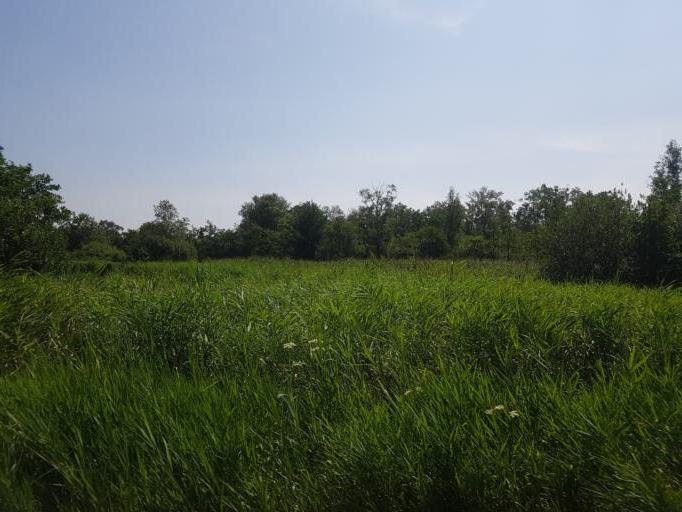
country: NL
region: Overijssel
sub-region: Gemeente Steenwijkerland
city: Giethoorn
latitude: 52.7666
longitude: 6.0872
